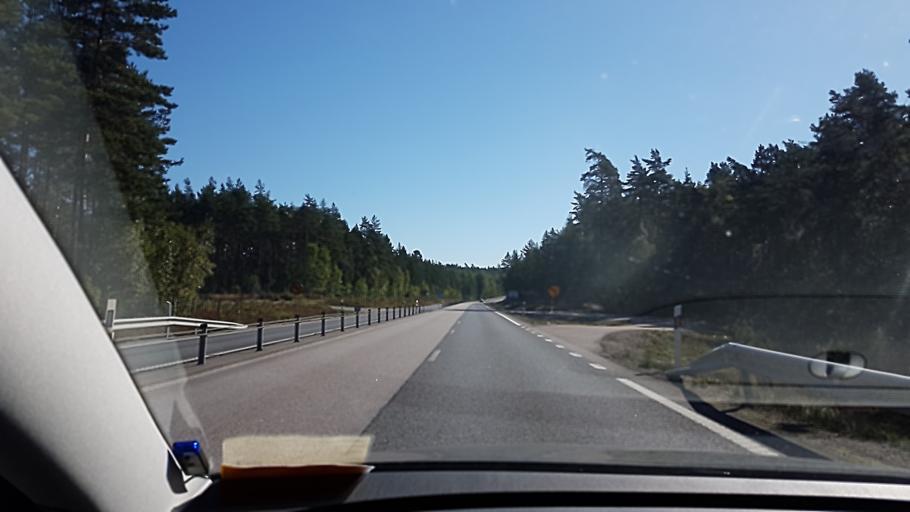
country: SE
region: Kronoberg
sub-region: Vaxjo Kommun
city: Vaexjoe
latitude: 56.8760
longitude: 14.9213
